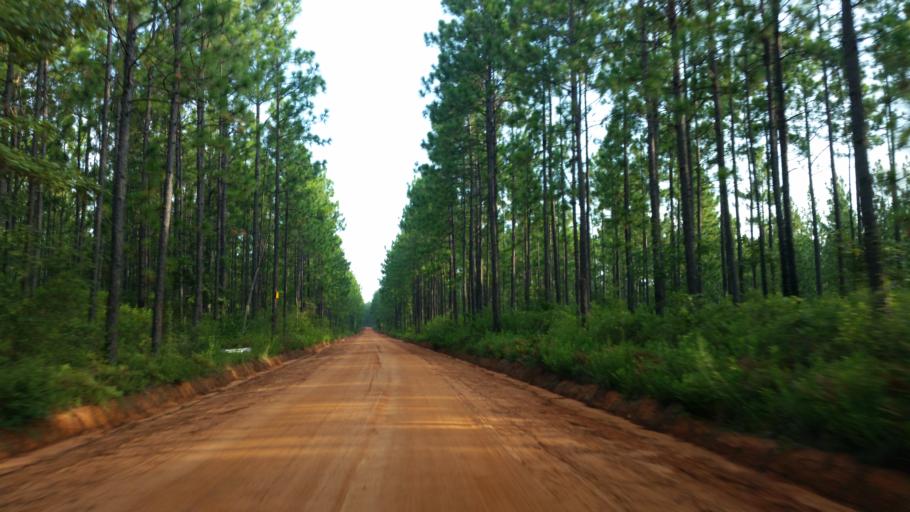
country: US
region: Alabama
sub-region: Escambia County
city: Atmore
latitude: 30.9306
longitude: -87.5699
